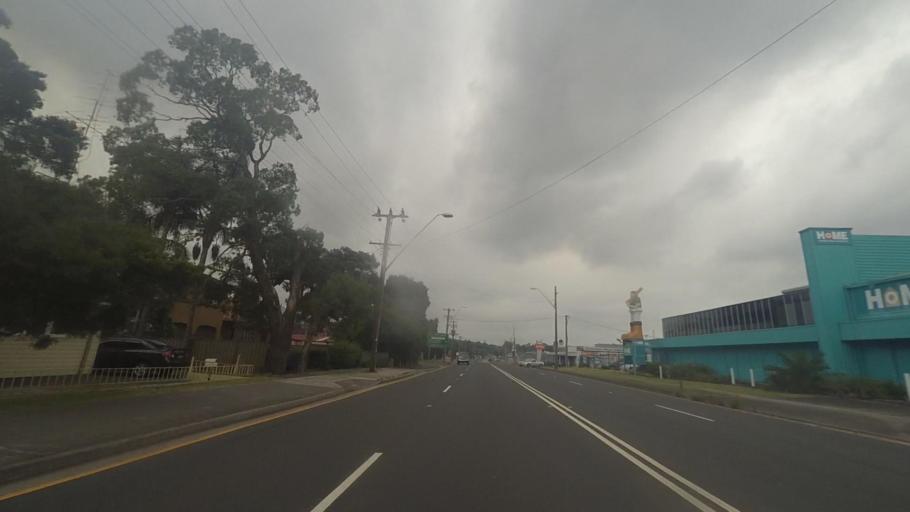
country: AU
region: New South Wales
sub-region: Wollongong
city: Cordeaux Heights
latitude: -34.4516
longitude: 150.8477
